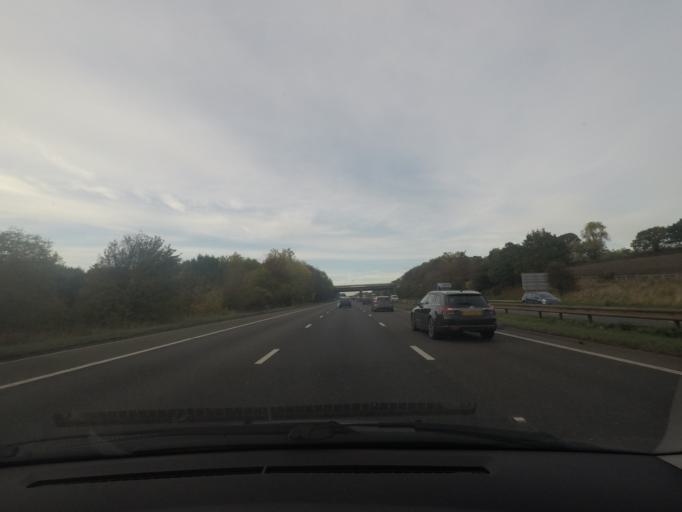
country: GB
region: England
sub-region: Barnsley
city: Stainborough
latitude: 53.5372
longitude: -1.5063
